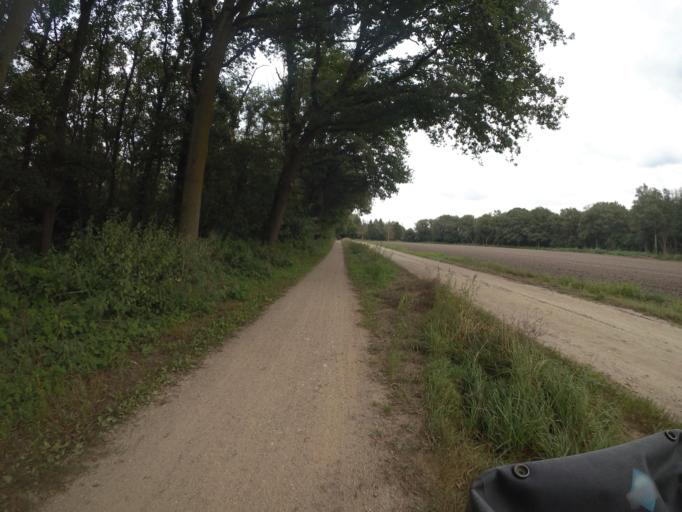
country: NL
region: Limburg
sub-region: Gemeente Gennep
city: Gennep
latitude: 51.6402
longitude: 6.0518
